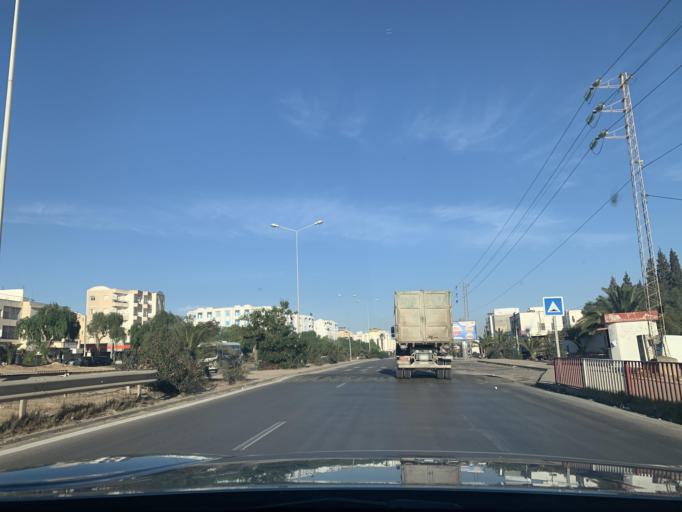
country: DZ
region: Souk Ahras
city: Souk Ahras
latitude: 36.3692
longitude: 7.9984
